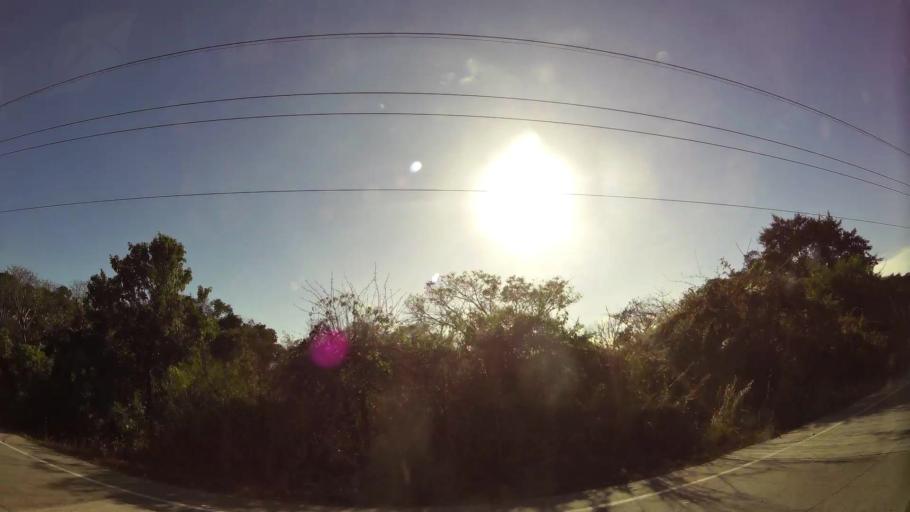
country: SV
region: Santa Ana
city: Metapan
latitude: 14.2378
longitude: -89.4704
